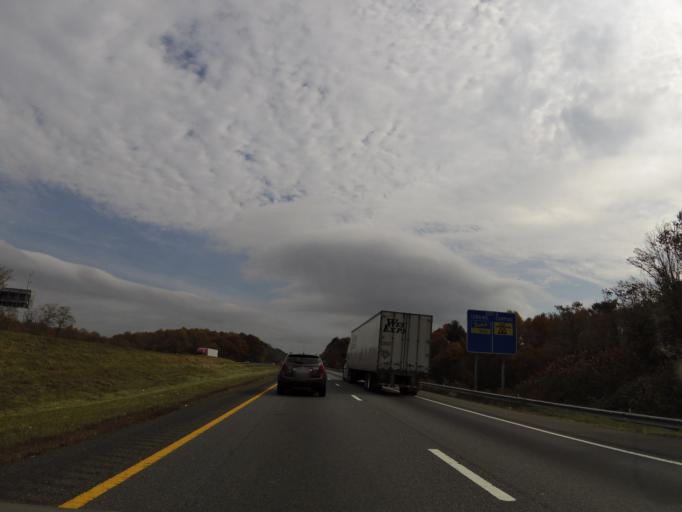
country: US
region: Virginia
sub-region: Carroll County
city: Hillsville
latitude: 36.6941
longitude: -80.7339
